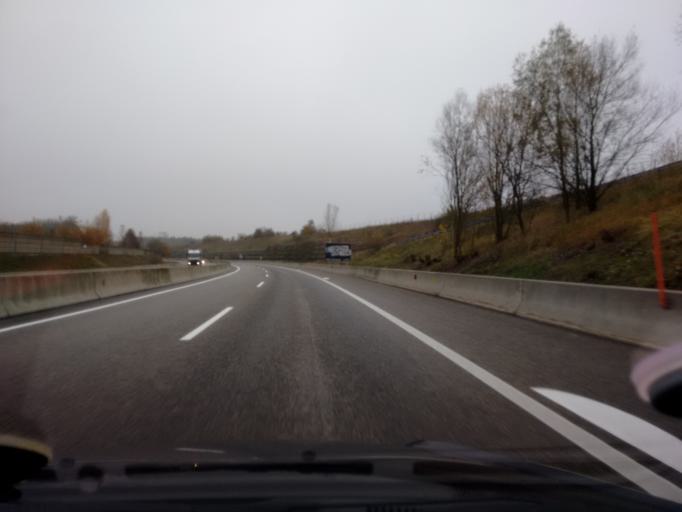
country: AT
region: Upper Austria
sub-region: Wels-Land
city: Steinhaus
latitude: 48.1254
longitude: 14.0048
